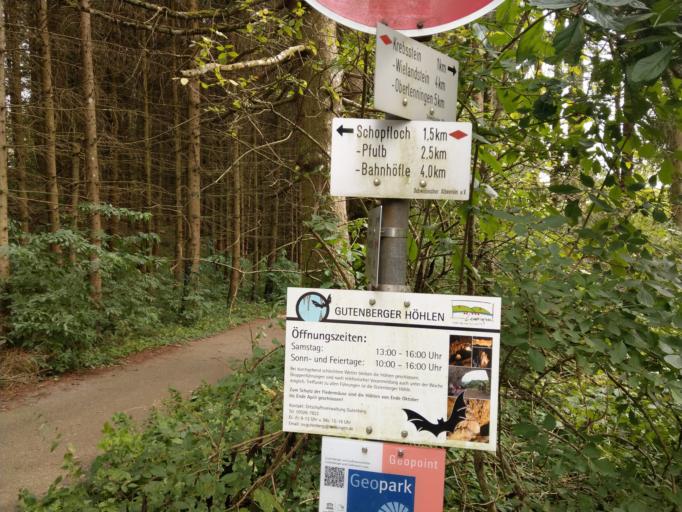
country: DE
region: Baden-Wuerttemberg
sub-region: Regierungsbezirk Stuttgart
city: Neidlingen
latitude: 48.5448
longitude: 9.5189
